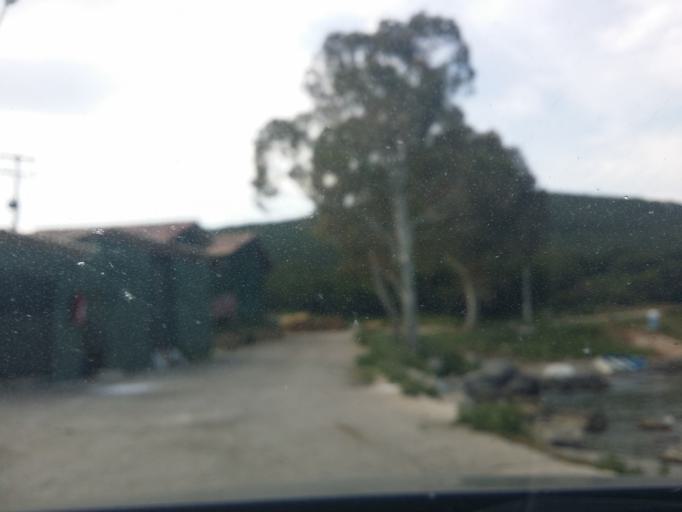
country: GR
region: Attica
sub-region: Nomos Piraios
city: Poros
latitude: 37.5459
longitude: 23.4787
